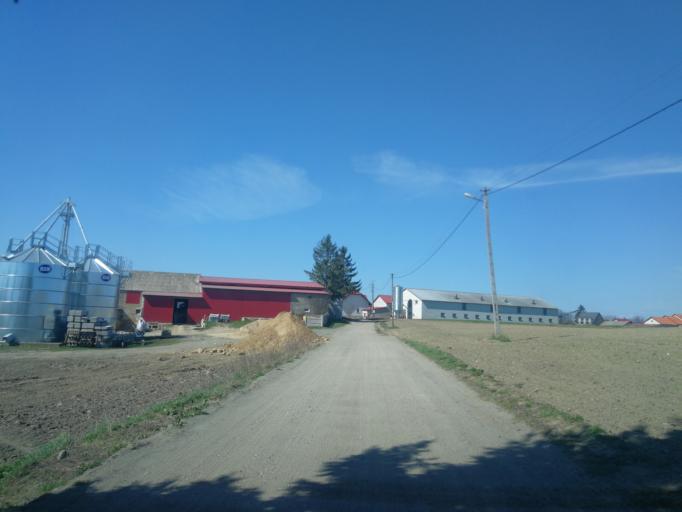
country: PL
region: Warmian-Masurian Voivodeship
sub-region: Powiat dzialdowski
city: Rybno
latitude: 53.4380
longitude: 19.9577
